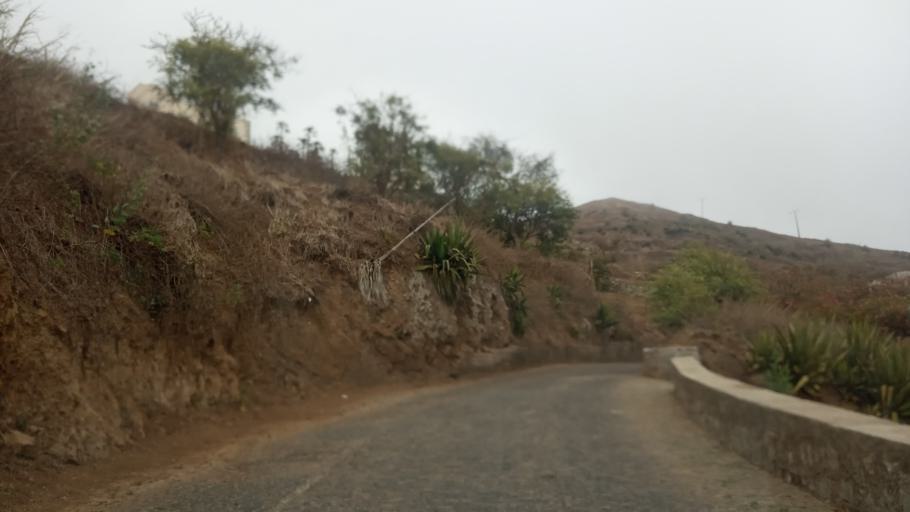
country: CV
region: Brava
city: Vila Nova Sintra
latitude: 14.8713
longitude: -24.7011
